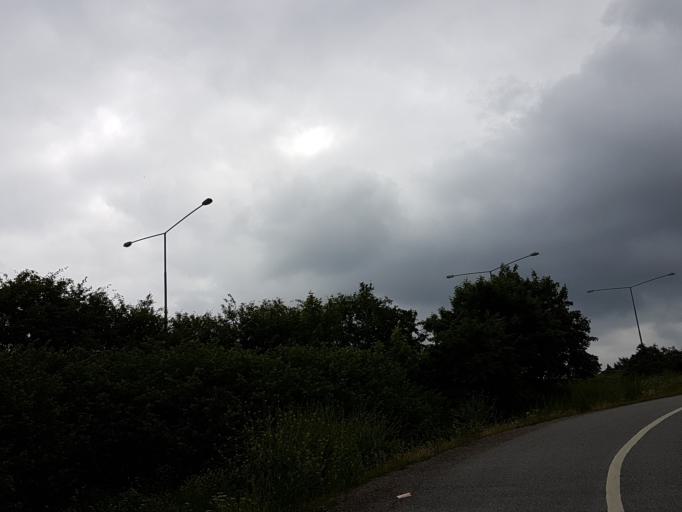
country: SE
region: Stockholm
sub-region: Sundbybergs Kommun
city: Sundbyberg
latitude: 59.3524
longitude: 17.9748
